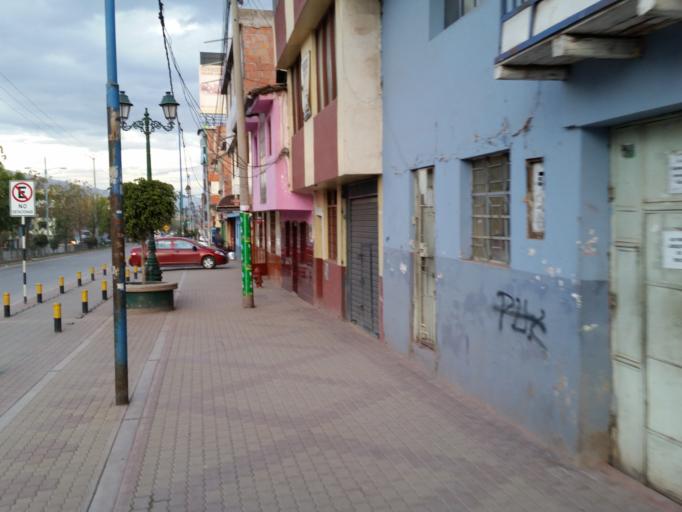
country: PE
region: Cusco
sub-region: Provincia de Cusco
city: Cusco
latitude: -13.5367
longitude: -71.9543
